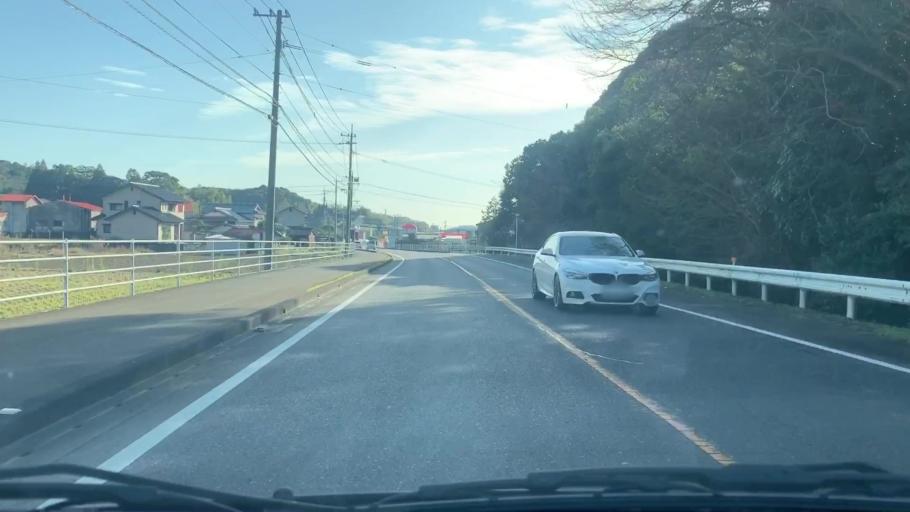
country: JP
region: Saga Prefecture
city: Takeocho-takeo
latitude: 33.2260
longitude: 130.0405
